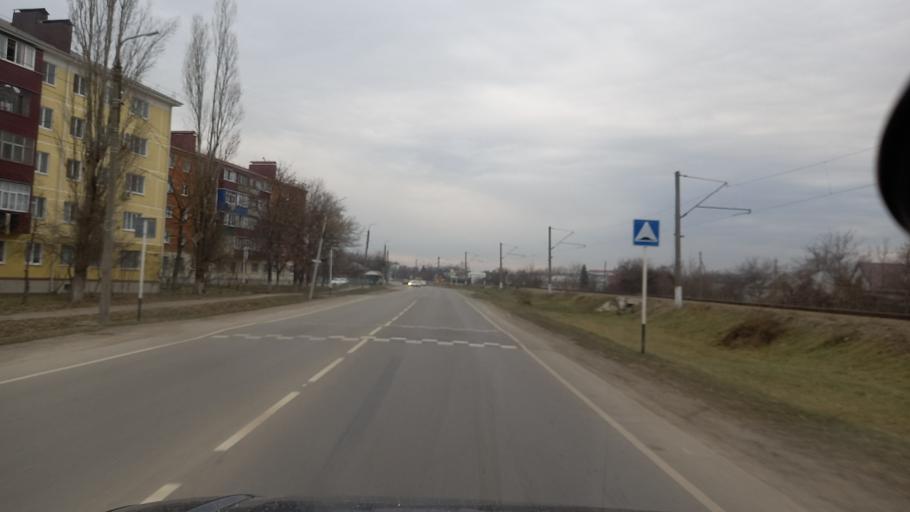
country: RU
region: Adygeya
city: Maykop
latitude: 44.5914
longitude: 40.1311
